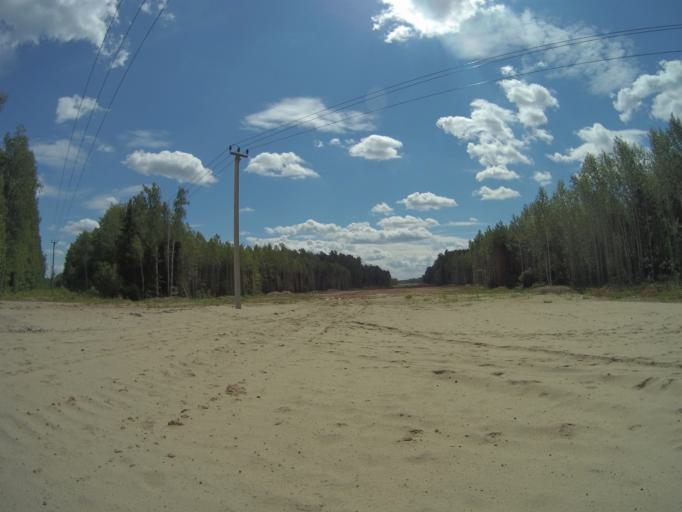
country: RU
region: Vladimir
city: Kommunar
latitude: 56.0547
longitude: 40.5120
